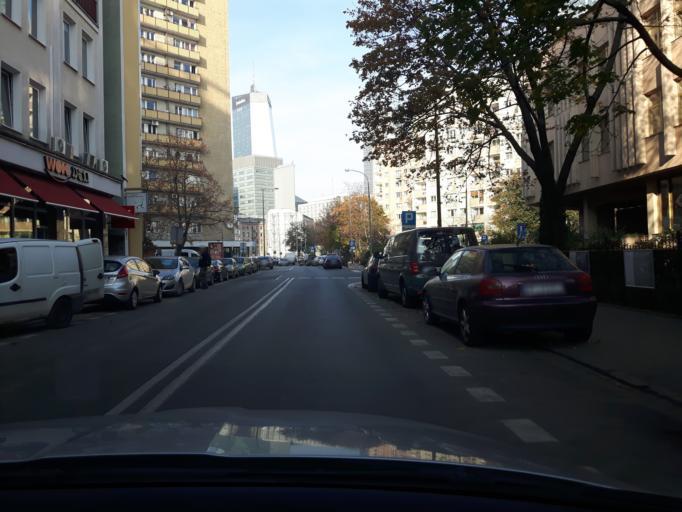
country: PL
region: Masovian Voivodeship
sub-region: Warszawa
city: Wola
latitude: 52.2310
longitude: 20.9957
